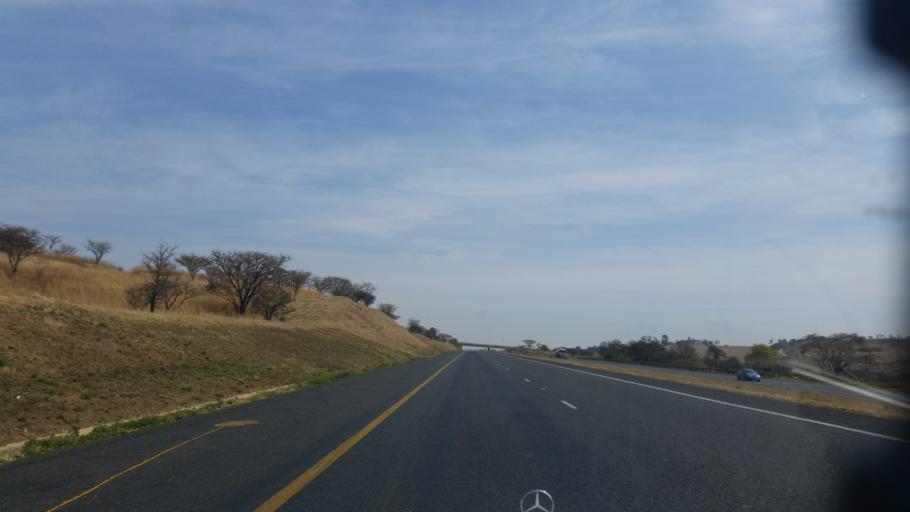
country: ZA
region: KwaZulu-Natal
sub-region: uThukela District Municipality
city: Estcourt
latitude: -29.0396
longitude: 29.8539
